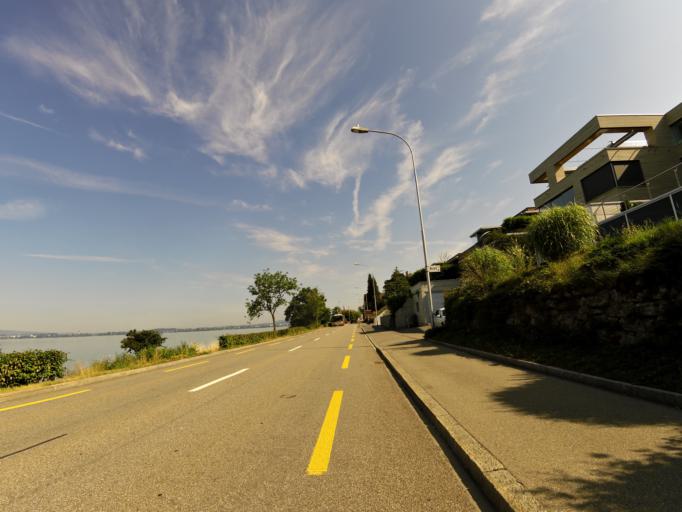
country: CH
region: Zug
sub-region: Zug
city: Zug
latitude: 47.1439
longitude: 8.5057
